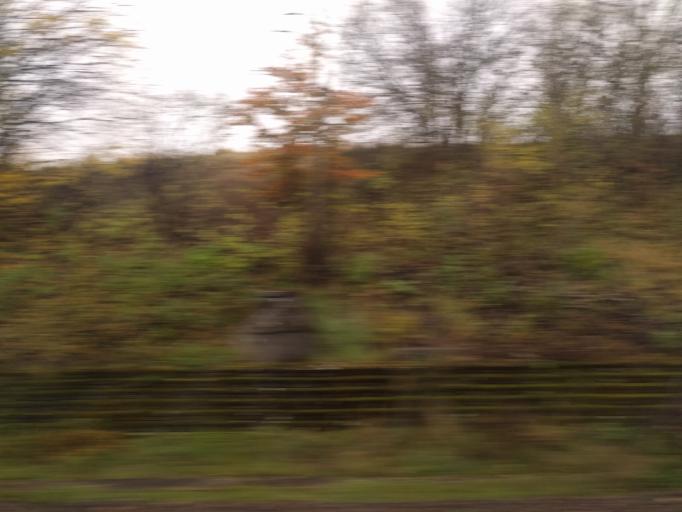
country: DK
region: Zealand
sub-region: Roskilde Kommune
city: Viby
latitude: 55.5727
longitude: 12.0355
